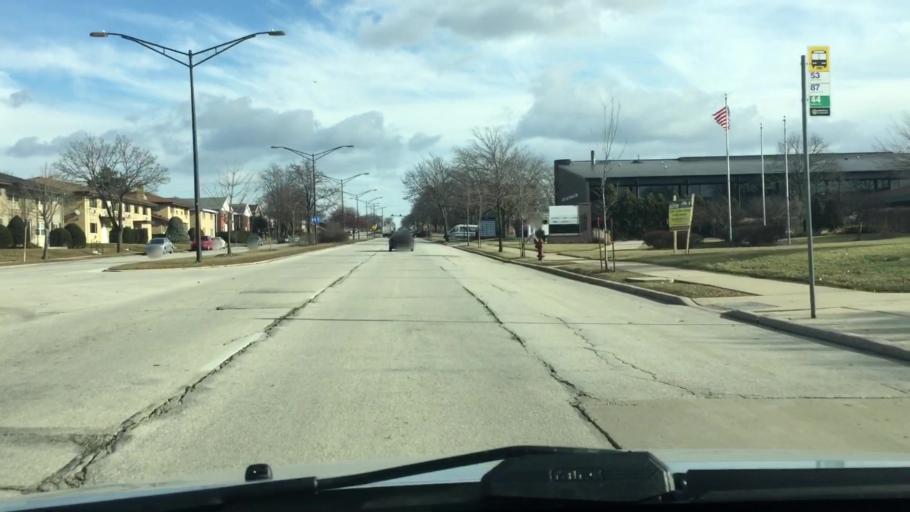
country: US
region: Wisconsin
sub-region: Milwaukee County
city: West Allis
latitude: 43.0025
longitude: -88.0434
